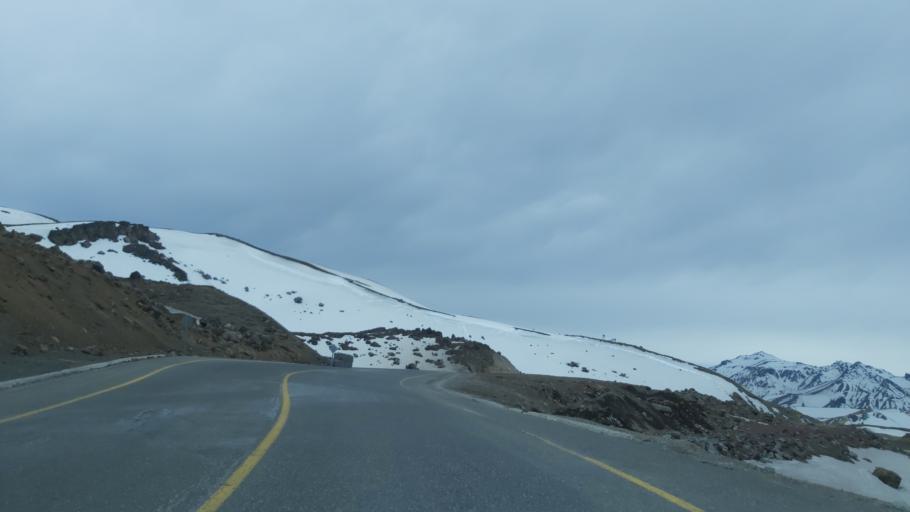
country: CL
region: Maule
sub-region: Provincia de Linares
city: Colbun
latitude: -35.9994
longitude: -70.5592
